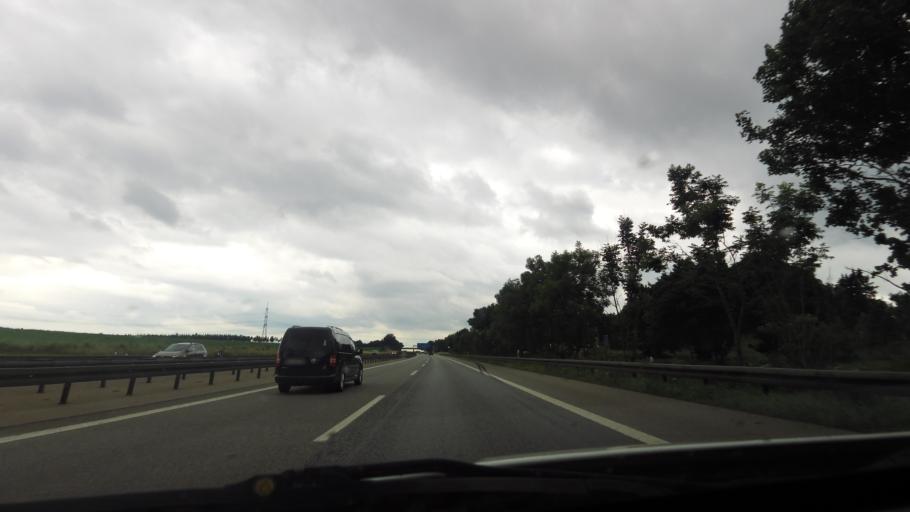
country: DE
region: Bavaria
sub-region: Swabia
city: Buxheim
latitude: 48.0138
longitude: 10.1379
